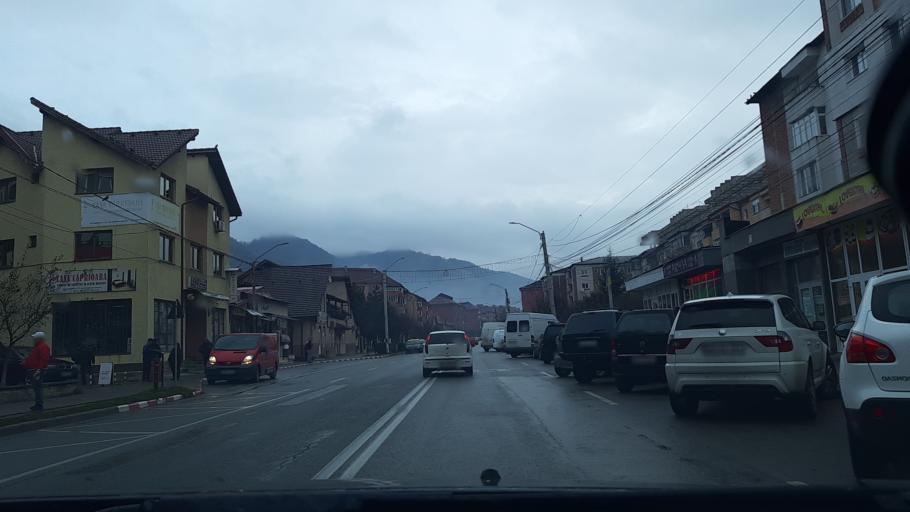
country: RO
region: Hunedoara
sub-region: Municipiul Petrosani
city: Petrosani
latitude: 45.4441
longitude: 23.3785
